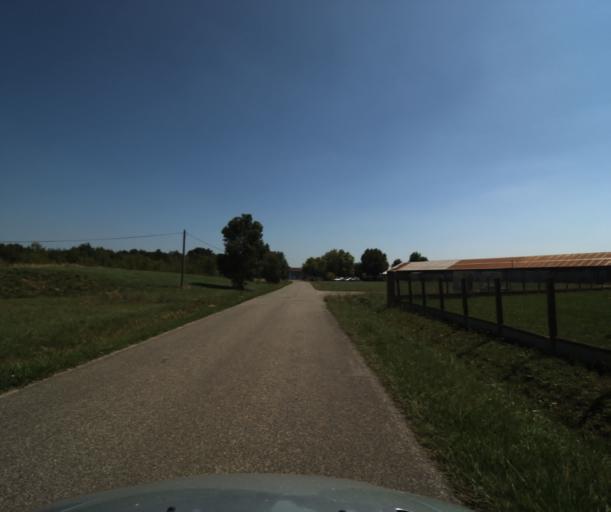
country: FR
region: Midi-Pyrenees
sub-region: Departement de la Haute-Garonne
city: Labastidette
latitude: 43.4497
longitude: 1.2689
